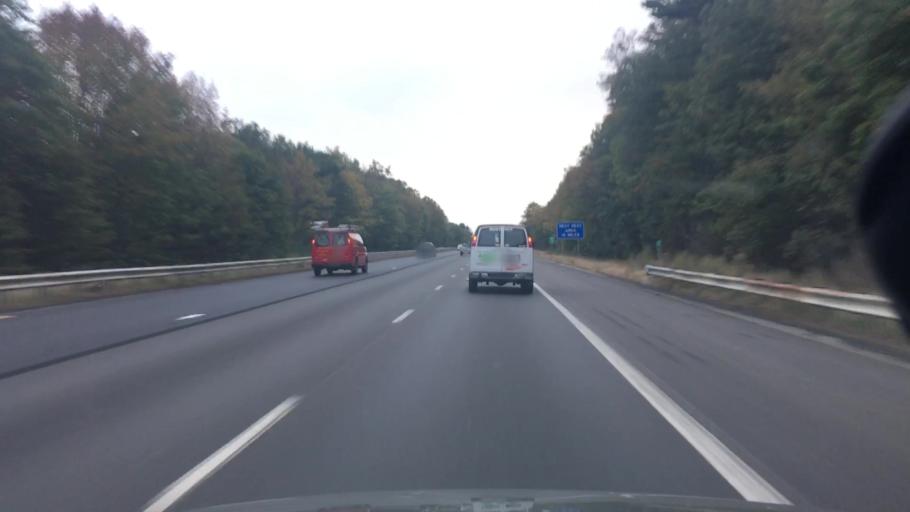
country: US
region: Massachusetts
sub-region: Hampden County
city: Holland
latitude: 42.0615
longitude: -72.1130
